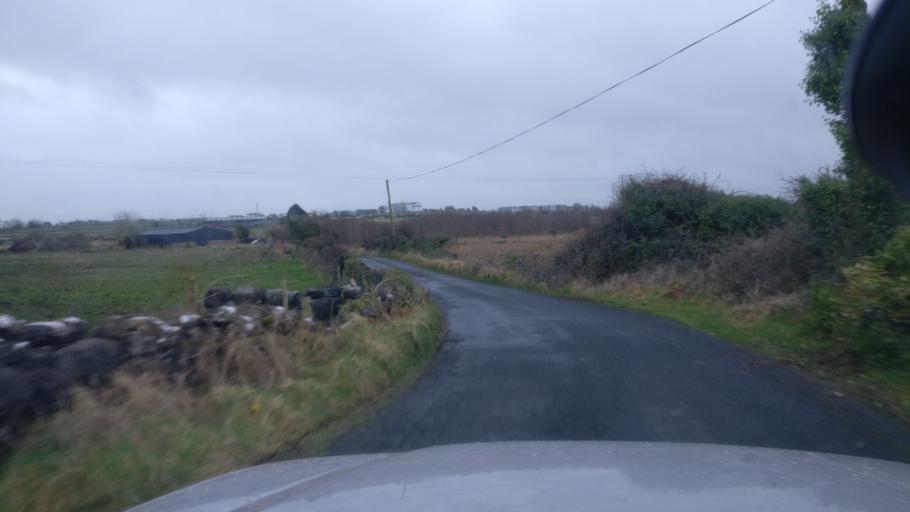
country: IE
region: Connaught
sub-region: County Galway
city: Loughrea
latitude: 53.2131
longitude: -8.5896
